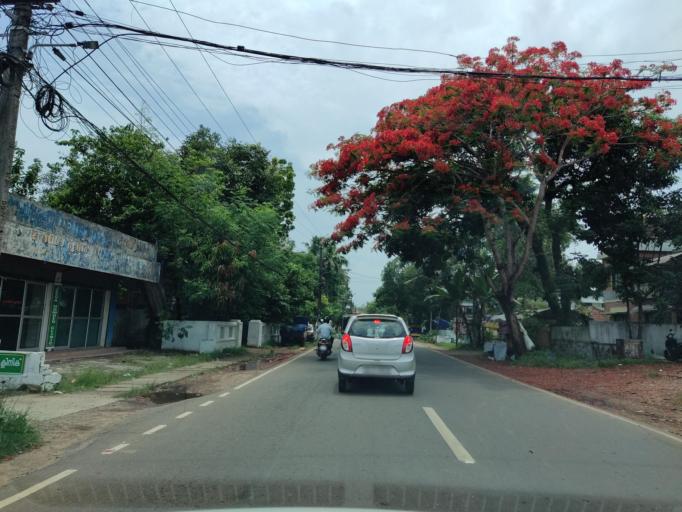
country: IN
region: Kerala
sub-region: Pattanamtitta
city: Adur
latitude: 9.2252
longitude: 76.6696
